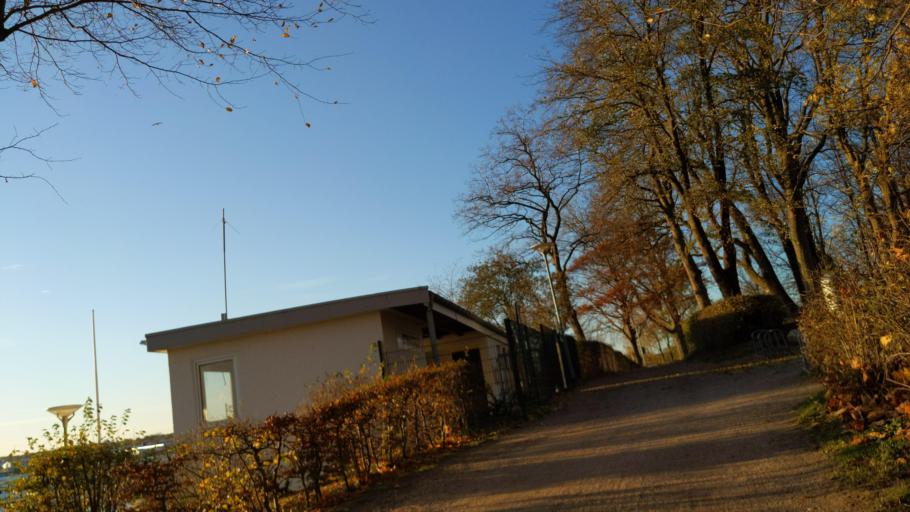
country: DE
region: Schleswig-Holstein
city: Neustadt in Holstein
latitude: 54.0927
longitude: 10.8158
